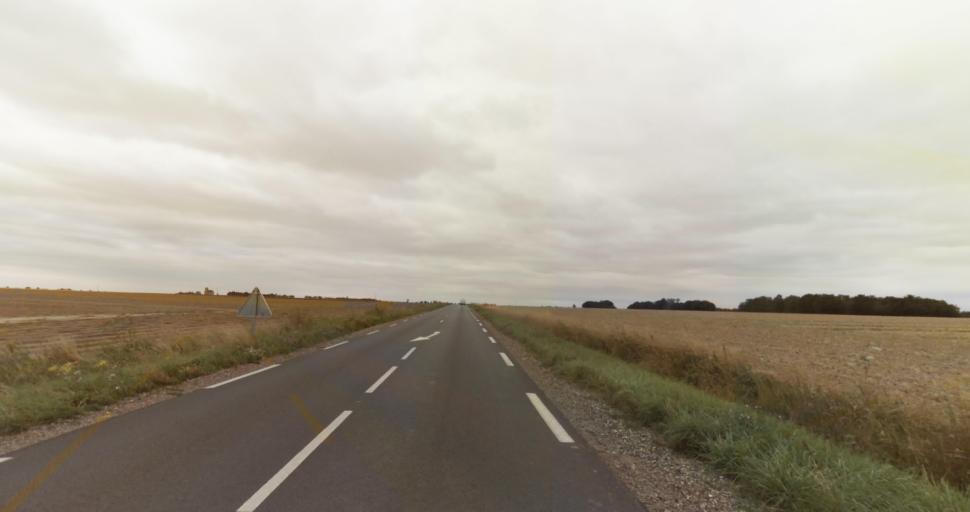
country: FR
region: Haute-Normandie
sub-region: Departement de l'Eure
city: Pacy-sur-Eure
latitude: 48.9611
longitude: 1.3197
